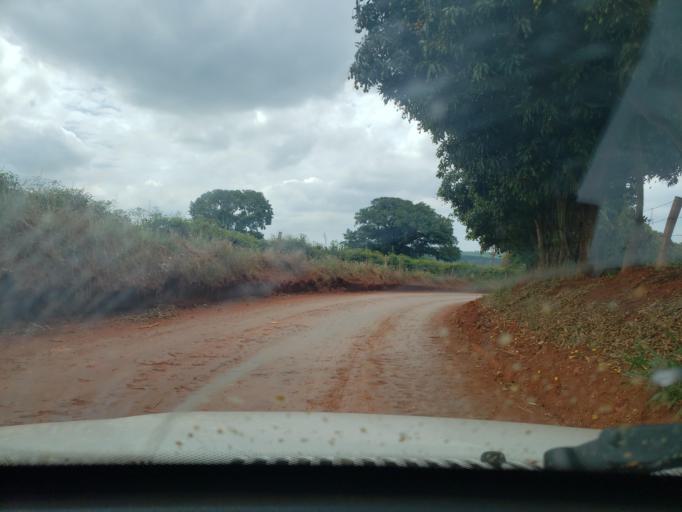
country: BR
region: Minas Gerais
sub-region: Boa Esperanca
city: Boa Esperanca
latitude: -20.9913
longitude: -45.5969
